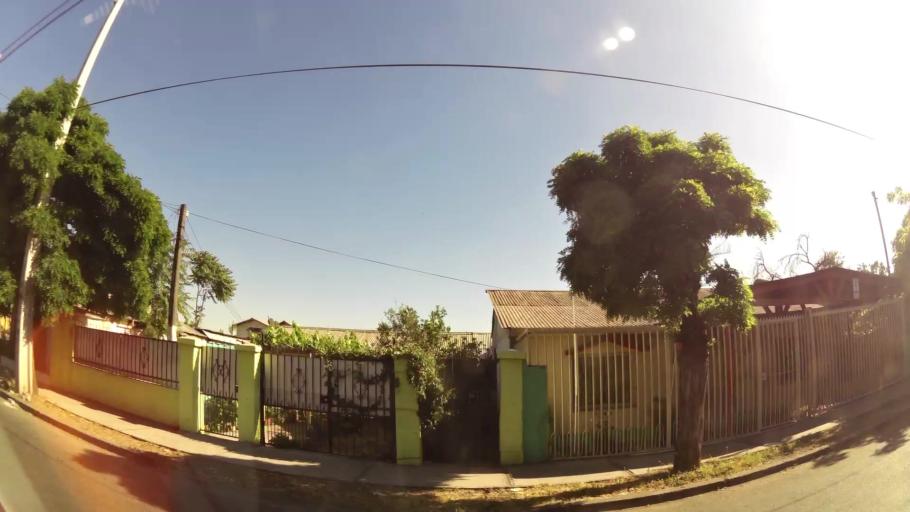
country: CL
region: Santiago Metropolitan
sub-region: Provincia de Maipo
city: San Bernardo
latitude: -33.5506
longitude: -70.6825
